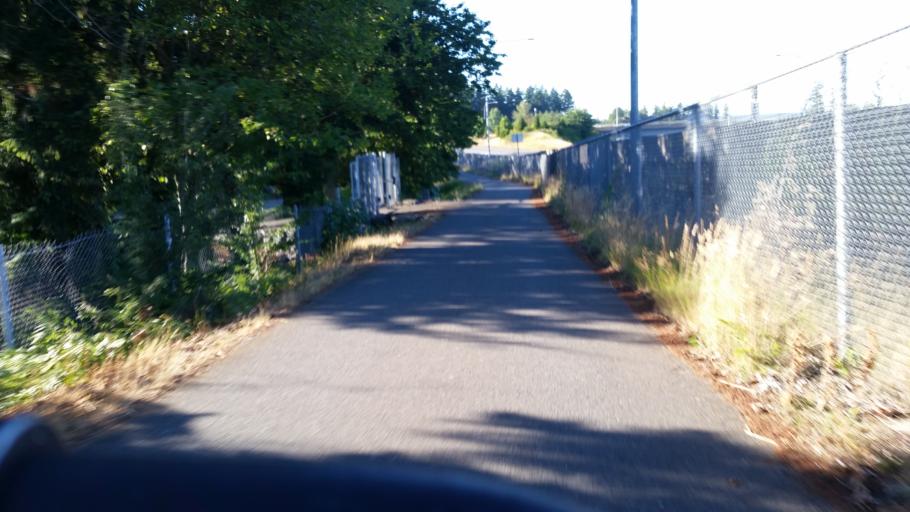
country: US
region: Washington
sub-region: King County
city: Redmond
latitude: 47.6524
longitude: -122.1382
